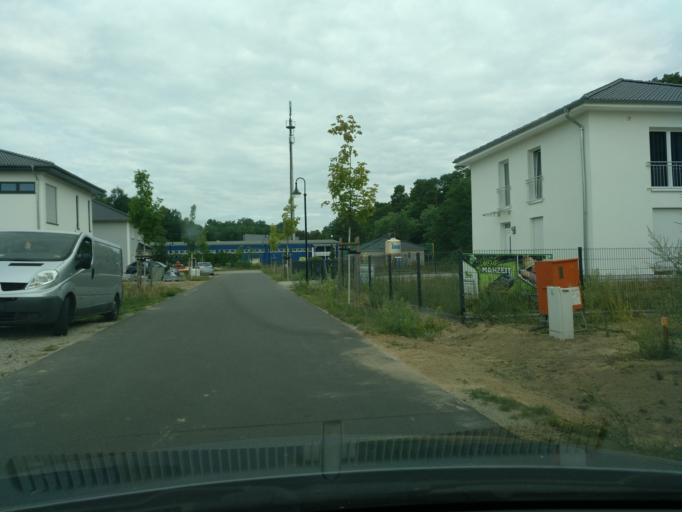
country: DE
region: Brandenburg
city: Bad Saarow
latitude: 52.2786
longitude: 14.0672
